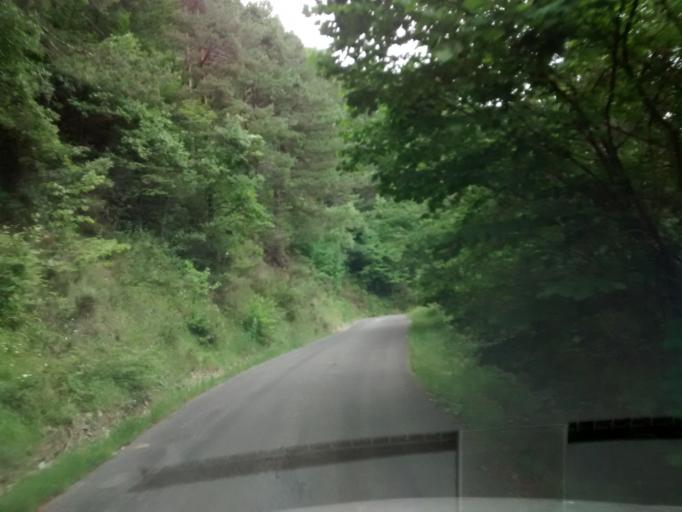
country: ES
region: Aragon
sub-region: Provincia de Huesca
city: Puertolas
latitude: 42.5708
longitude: 0.1394
